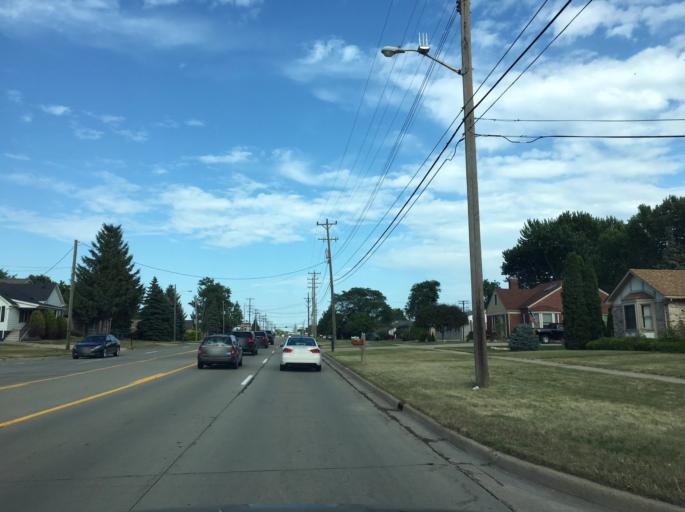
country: US
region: Michigan
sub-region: Macomb County
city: Fraser
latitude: 42.5390
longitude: -82.9425
